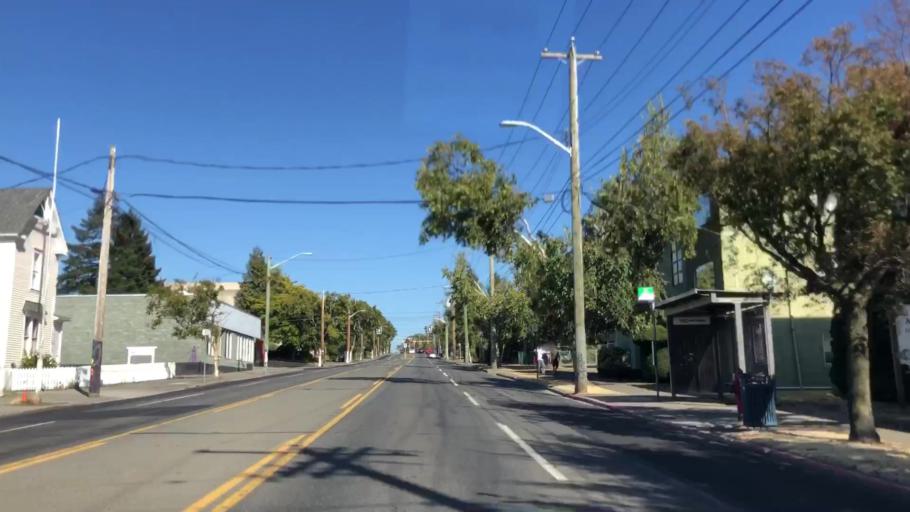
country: CA
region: British Columbia
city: Victoria
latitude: 48.4398
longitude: -123.3563
